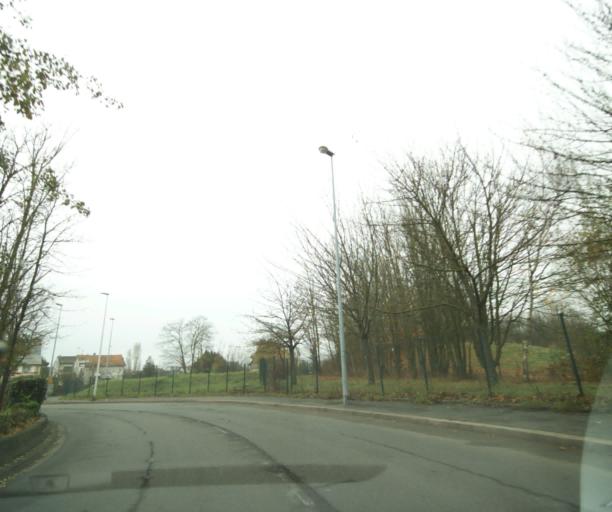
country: FR
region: Ile-de-France
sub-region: Departement de Seine-Saint-Denis
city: Livry-Gargan
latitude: 48.9343
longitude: 2.5429
